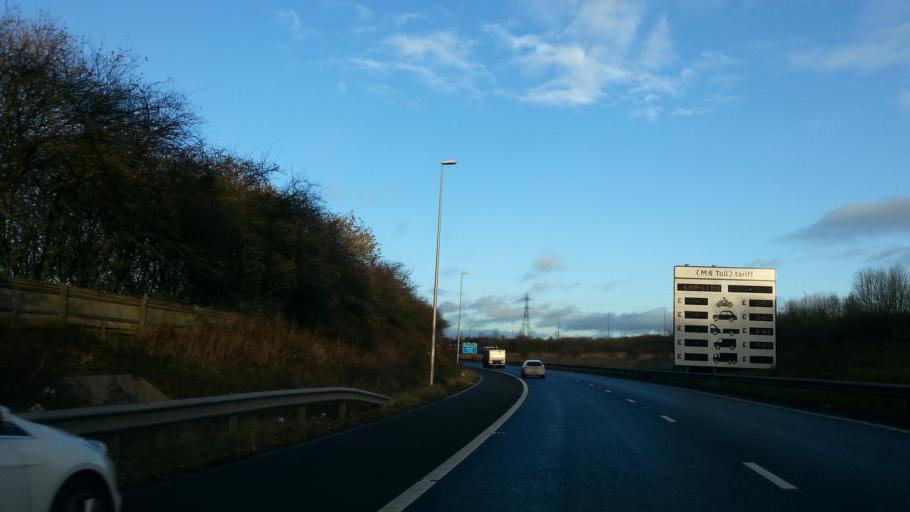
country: GB
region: England
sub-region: Warwickshire
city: Water Orton
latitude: 52.5086
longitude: -1.7307
